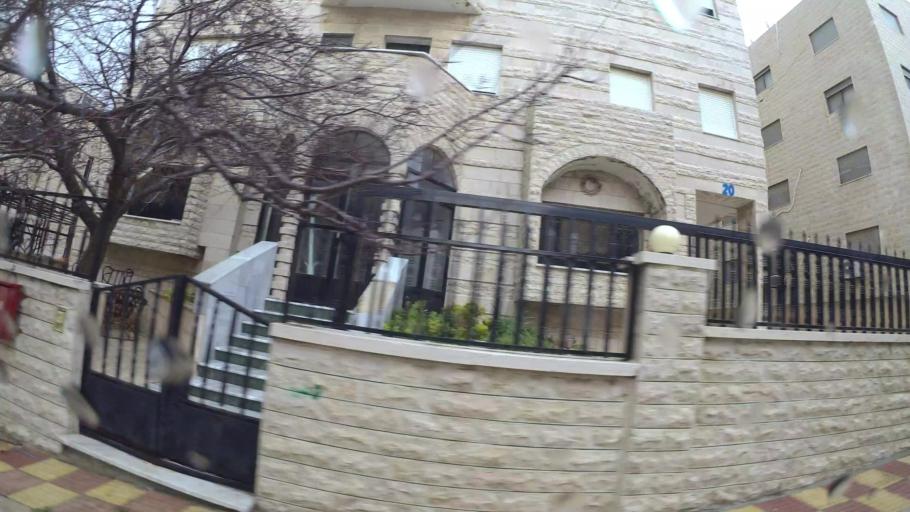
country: JO
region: Amman
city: Al Jubayhah
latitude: 32.0303
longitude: 35.8776
